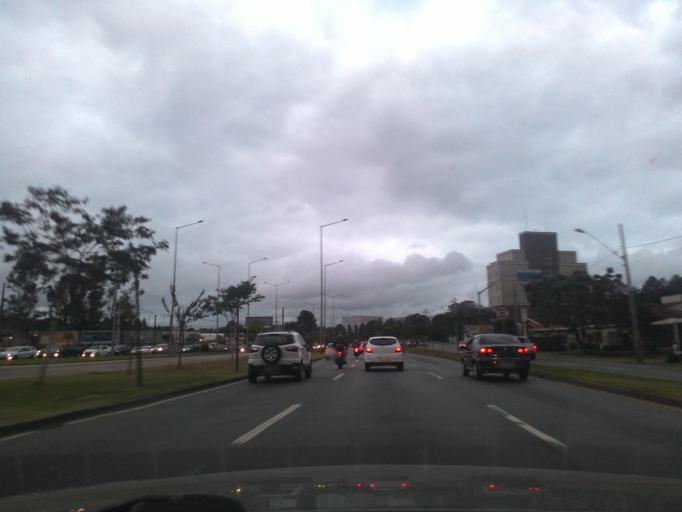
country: BR
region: Parana
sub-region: Curitiba
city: Curitiba
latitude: -25.4532
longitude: -49.2425
